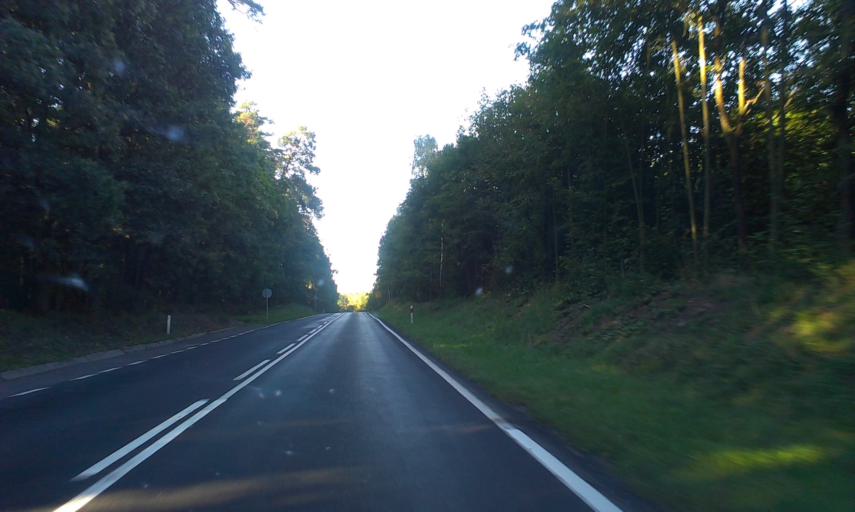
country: PL
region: Kujawsko-Pomorskie
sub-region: Powiat tucholski
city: Tuchola
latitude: 53.5568
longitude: 17.9014
